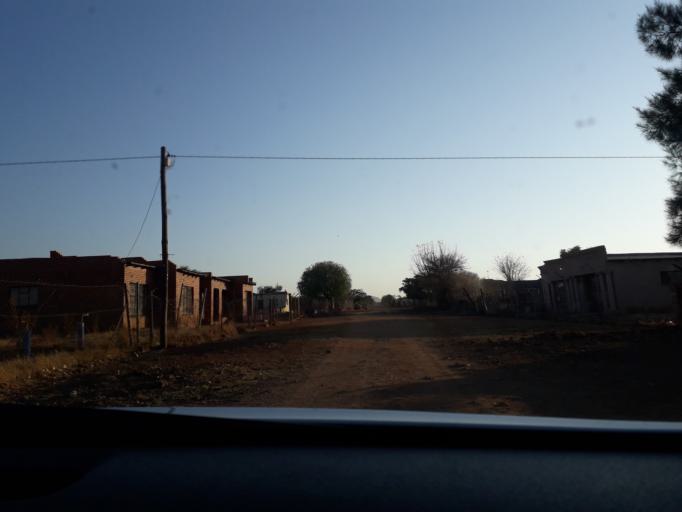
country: ZA
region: Limpopo
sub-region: Waterberg District Municipality
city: Mokopane
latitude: -23.9150
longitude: 28.8700
